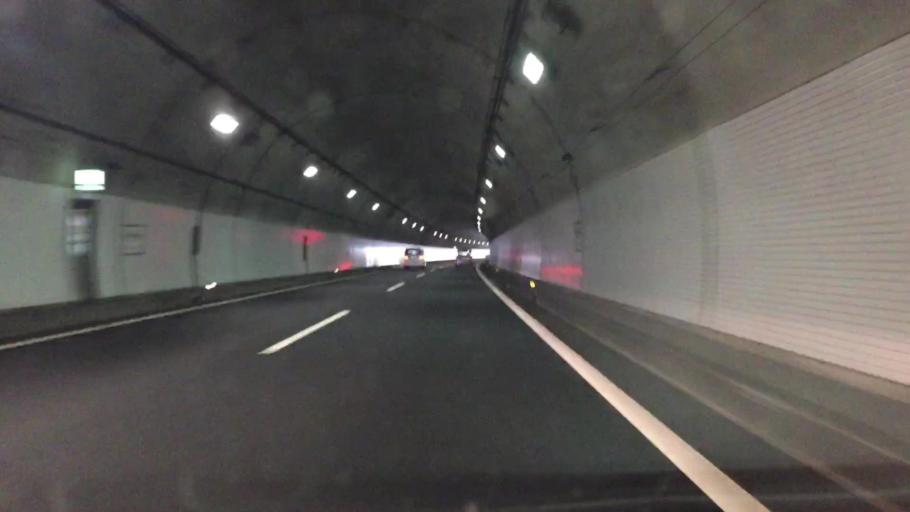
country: JP
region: Tochigi
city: Ashikaga
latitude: 36.3682
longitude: 139.4643
